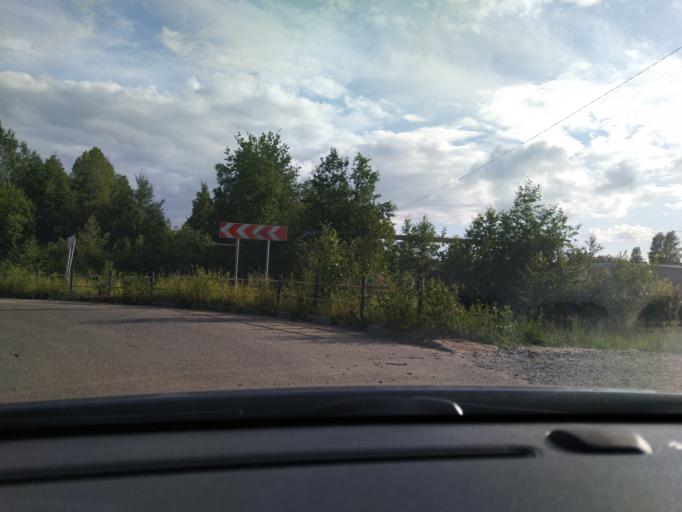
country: RU
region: St.-Petersburg
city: Gorelovo
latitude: 59.7845
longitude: 30.1650
